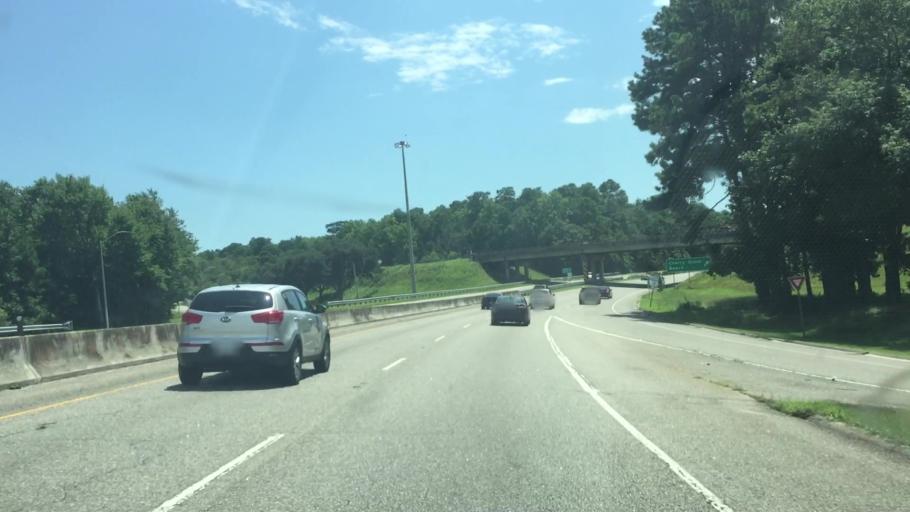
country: US
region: South Carolina
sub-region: Horry County
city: North Myrtle Beach
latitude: 33.8490
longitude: -78.6527
